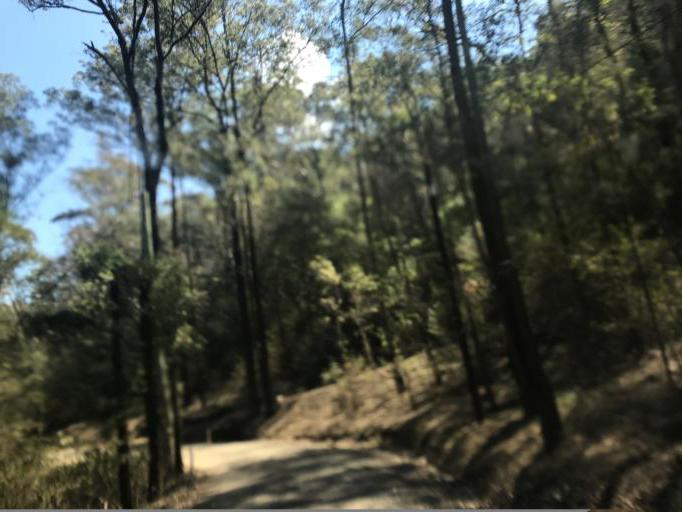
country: AU
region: New South Wales
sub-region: Hawkesbury
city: Pitt Town
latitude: -33.4169
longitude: 150.9113
